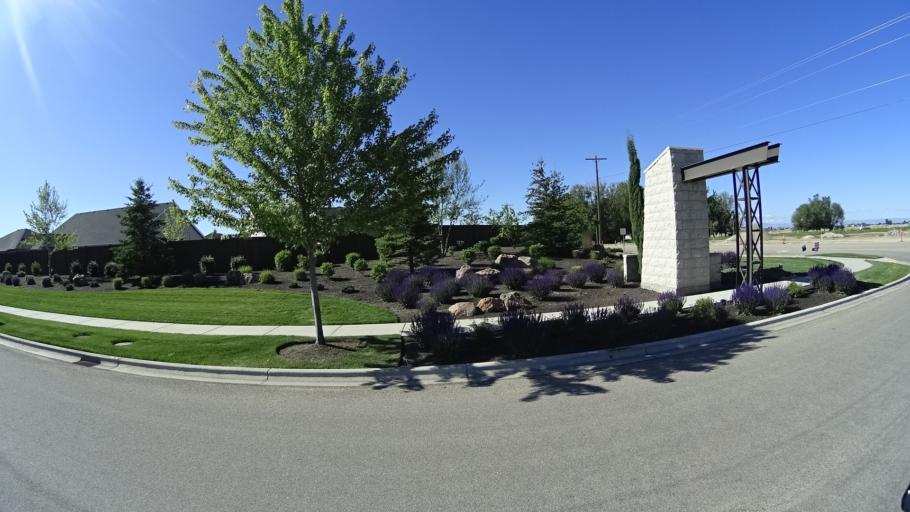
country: US
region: Idaho
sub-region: Ada County
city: Star
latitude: 43.6580
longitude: -116.4531
